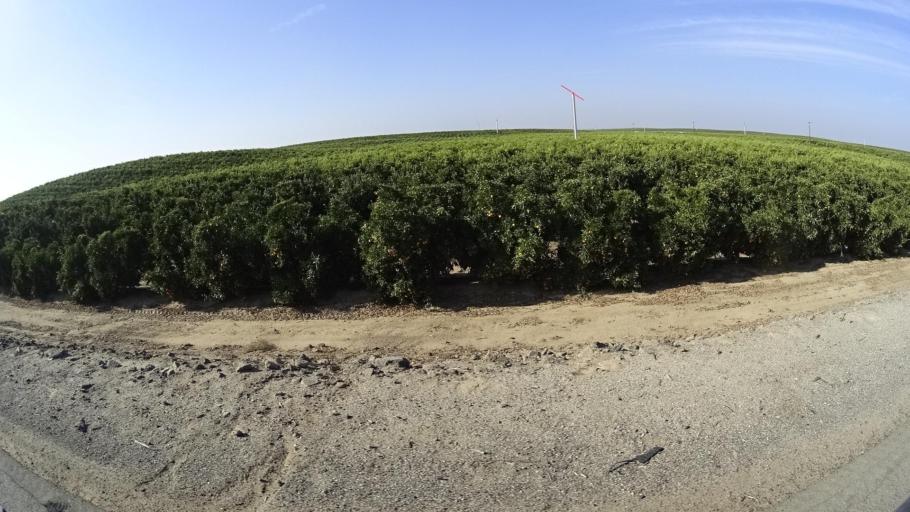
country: US
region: California
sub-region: Kern County
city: McFarland
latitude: 35.6481
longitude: -119.1337
